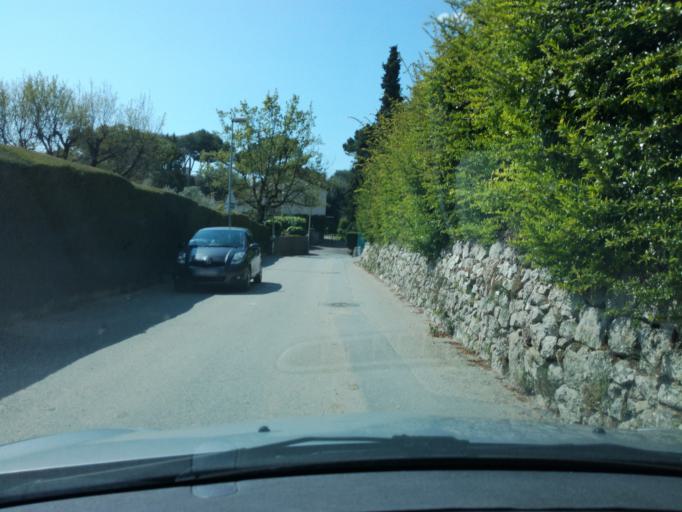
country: FR
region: Provence-Alpes-Cote d'Azur
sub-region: Departement des Alpes-Maritimes
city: Mougins
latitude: 43.6086
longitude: 6.9916
